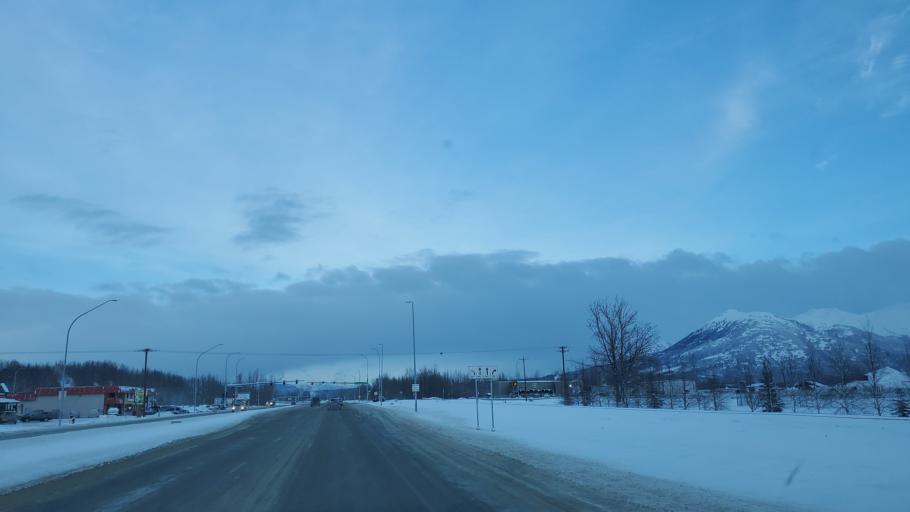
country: US
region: Alaska
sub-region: Matanuska-Susitna Borough
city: Palmer
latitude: 61.5839
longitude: -149.1320
